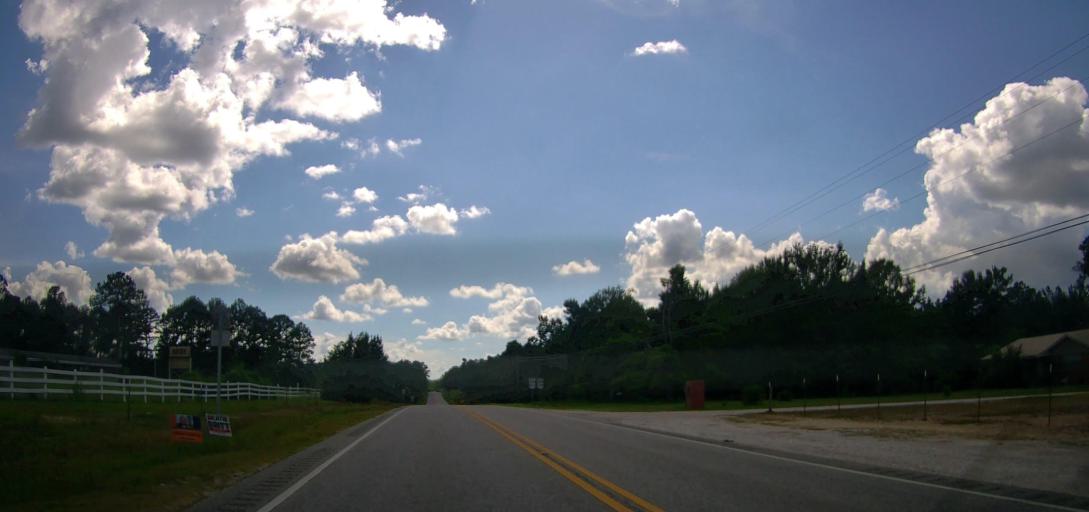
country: US
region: Alabama
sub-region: Macon County
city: Tuskegee
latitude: 32.4639
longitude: -85.6003
